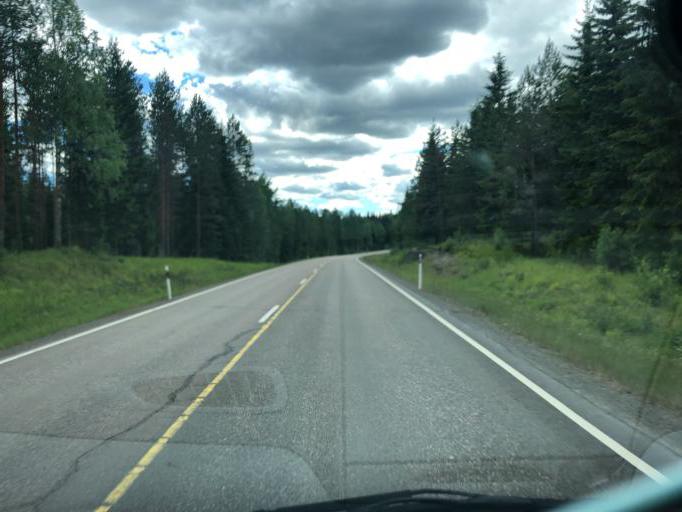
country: FI
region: Kymenlaakso
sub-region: Kouvola
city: Kouvola
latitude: 61.0455
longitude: 27.0184
